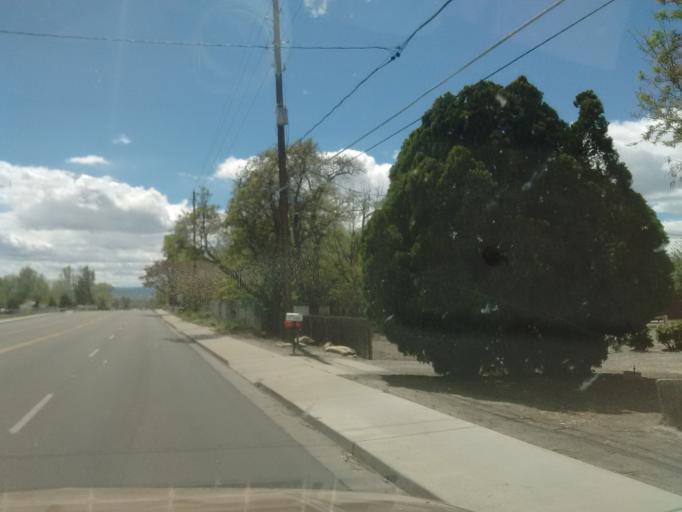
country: US
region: Colorado
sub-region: Mesa County
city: Fruitvale
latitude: 39.0844
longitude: -108.4967
